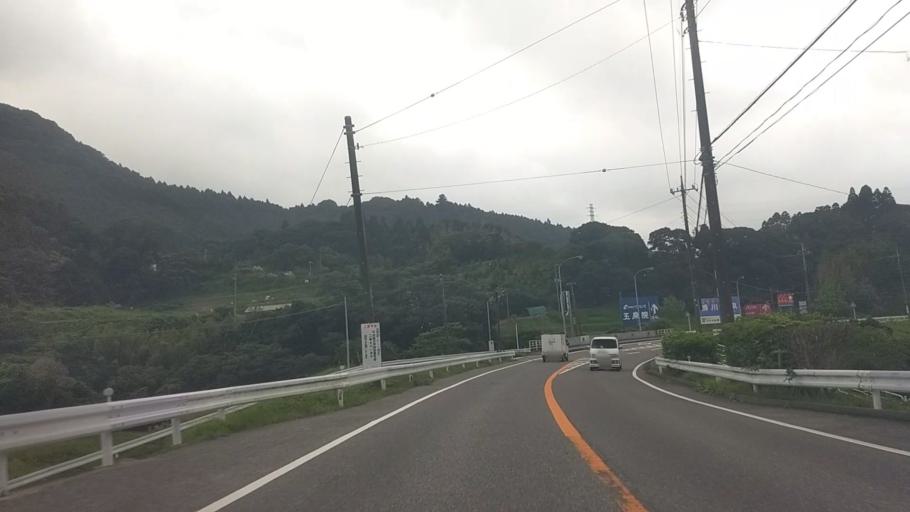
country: JP
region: Chiba
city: Kawaguchi
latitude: 35.1443
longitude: 140.0694
